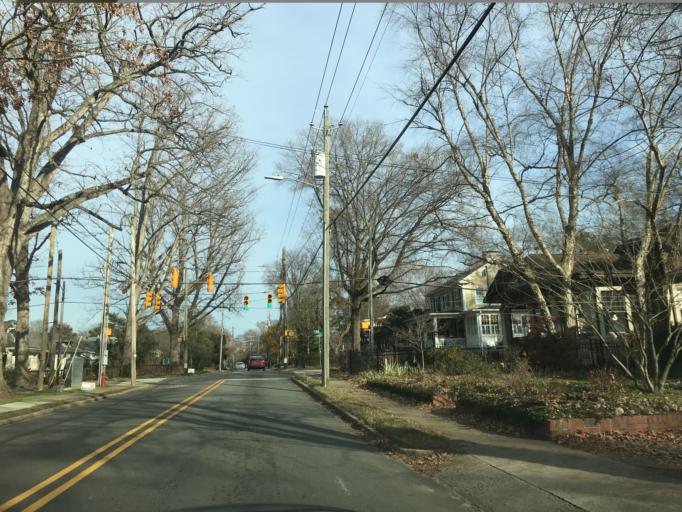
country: US
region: North Carolina
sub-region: Wake County
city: West Raleigh
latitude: 35.8048
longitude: -78.6437
